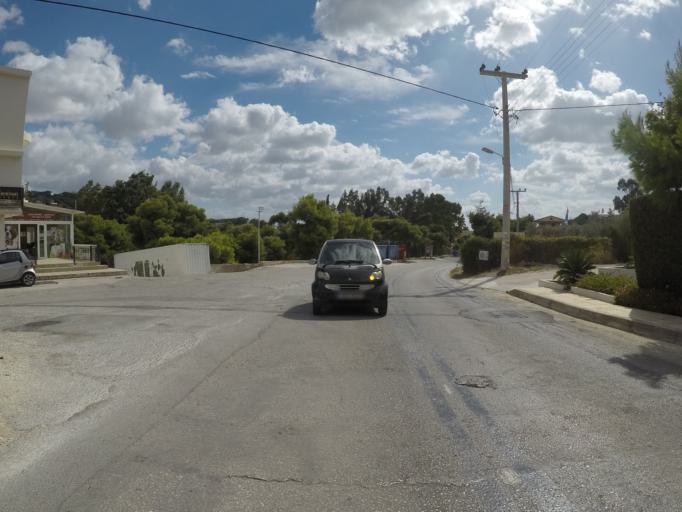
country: GR
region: Attica
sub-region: Nomarchia Anatolikis Attikis
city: Agios Dimitrios Kropias
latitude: 37.8070
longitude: 23.8685
